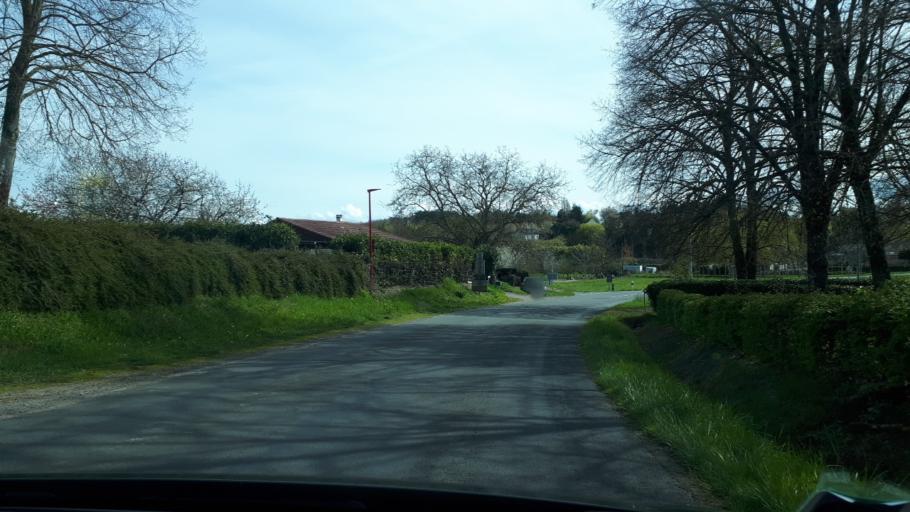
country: FR
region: Pays de la Loire
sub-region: Departement de la Sarthe
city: Yvre-le-Polin
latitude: 47.8224
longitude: 0.1565
